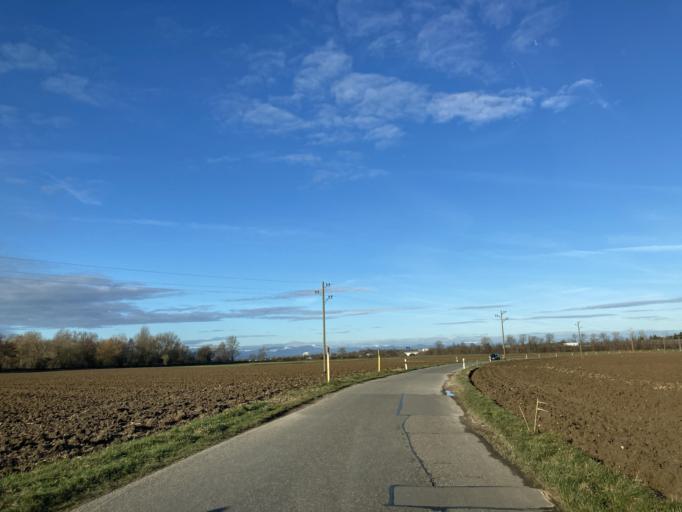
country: DE
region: Baden-Wuerttemberg
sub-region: Freiburg Region
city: Unterkrozingen
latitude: 47.9496
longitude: 7.6809
